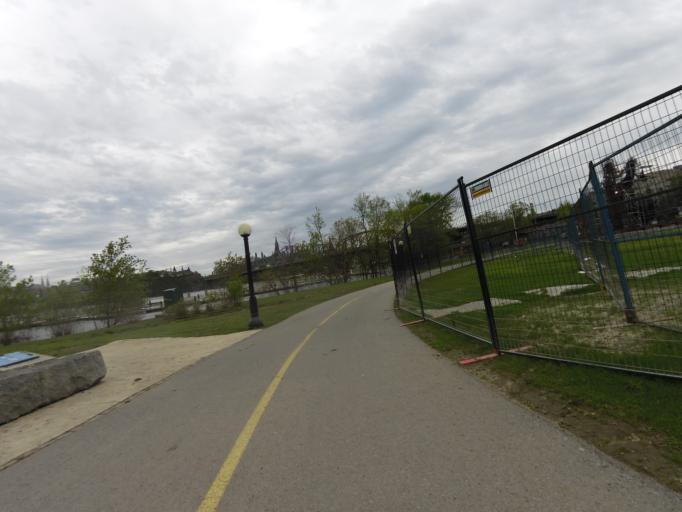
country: CA
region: Ontario
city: Ottawa
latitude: 45.4331
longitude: -75.7073
